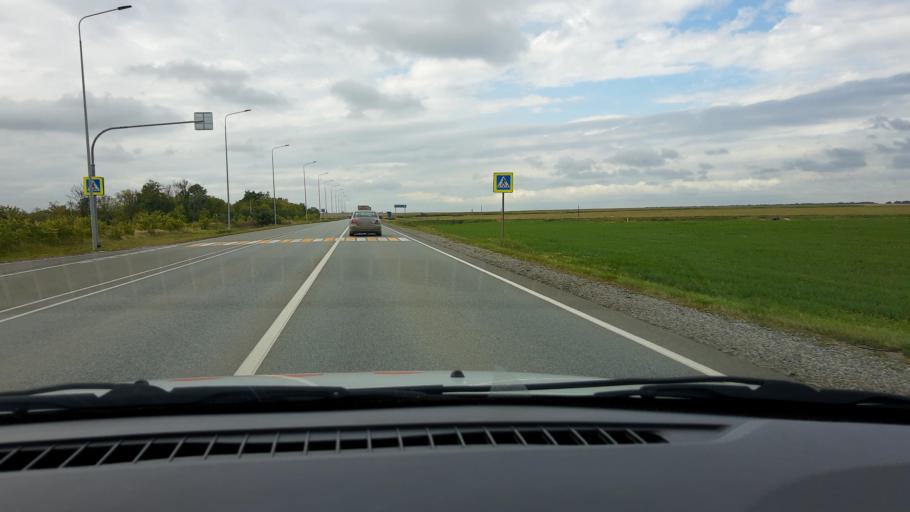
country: RU
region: Tatarstan
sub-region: Alekseyevskiy Rayon
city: Alekseyevskoye
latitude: 55.3136
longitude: 50.2868
